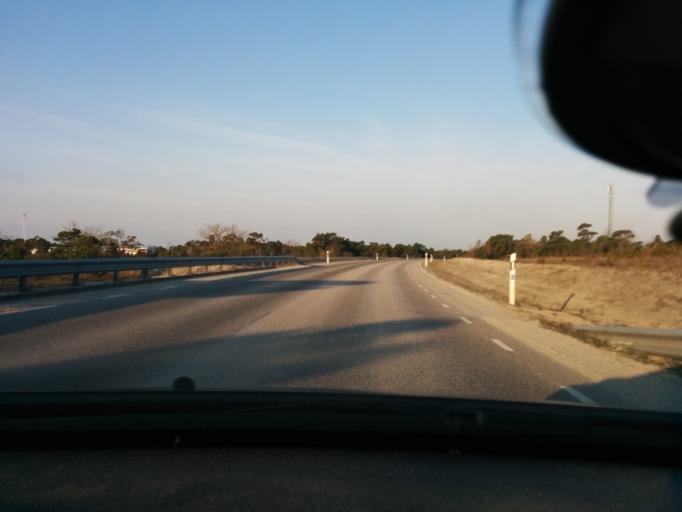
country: SE
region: Gotland
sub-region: Gotland
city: Visby
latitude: 57.6316
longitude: 18.3558
